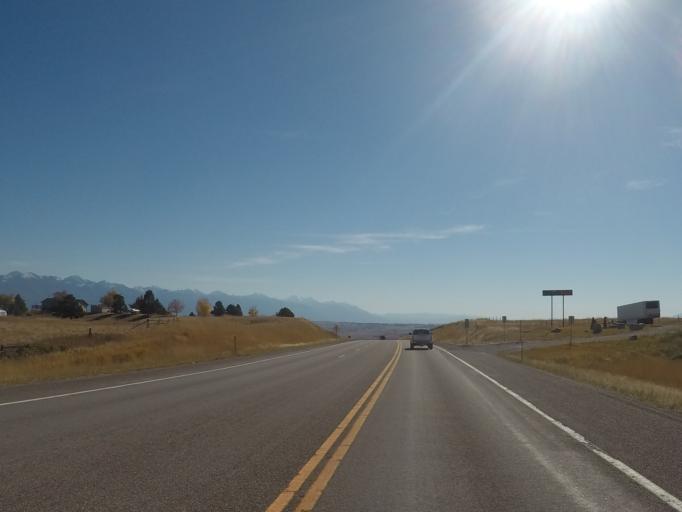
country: US
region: Montana
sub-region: Lake County
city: Polson
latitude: 47.7444
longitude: -114.2289
